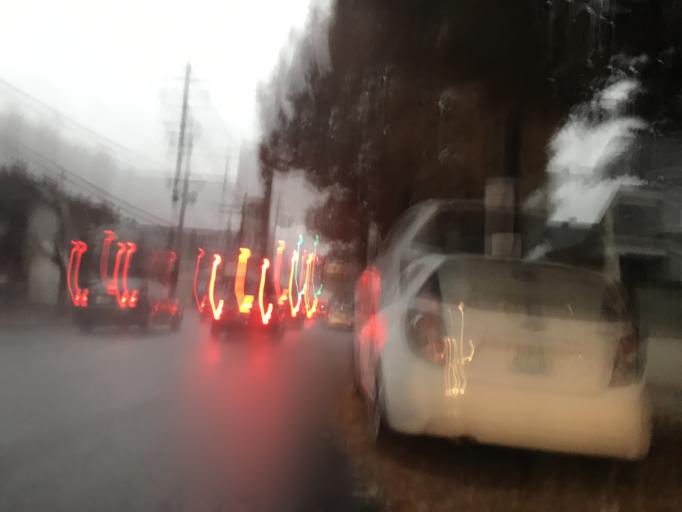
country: US
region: Kentucky
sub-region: Jefferson County
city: Louisville
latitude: 38.2345
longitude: -85.7414
